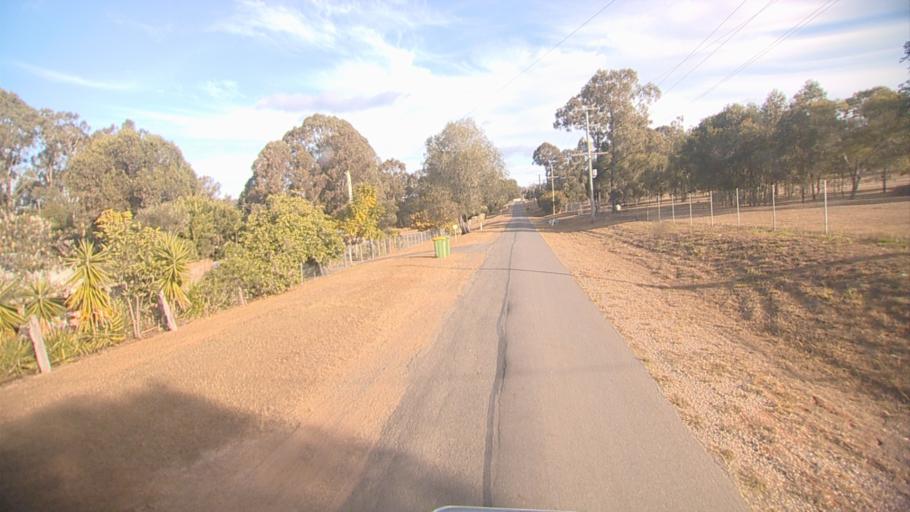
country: AU
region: Queensland
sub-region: Logan
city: Cedar Vale
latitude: -27.8798
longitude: 153.0210
